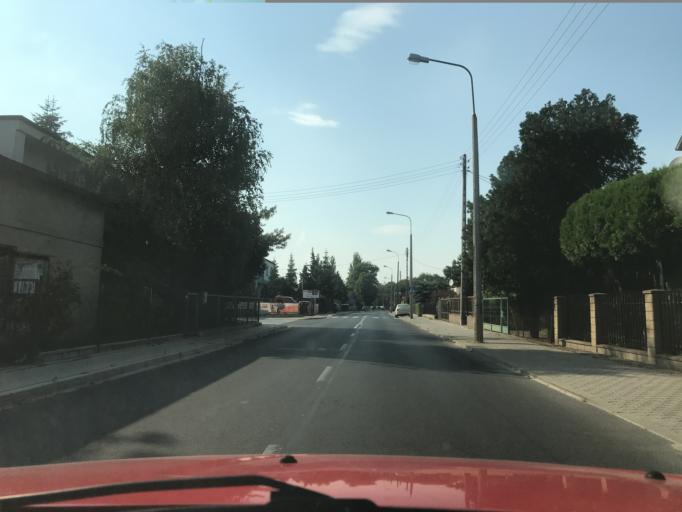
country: PL
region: Greater Poland Voivodeship
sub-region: Powiat poznanski
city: Plewiska
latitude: 52.3670
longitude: 16.8503
